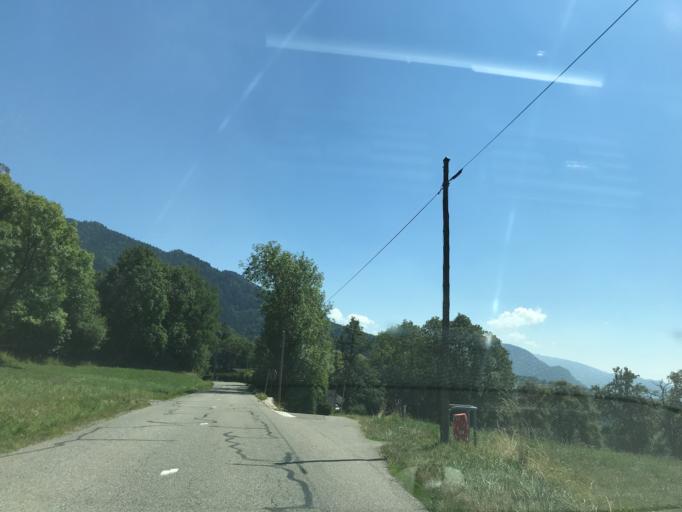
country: FR
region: Rhone-Alpes
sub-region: Departement de la Haute-Savoie
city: Thorens-Glieres
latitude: 45.9732
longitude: 6.2175
